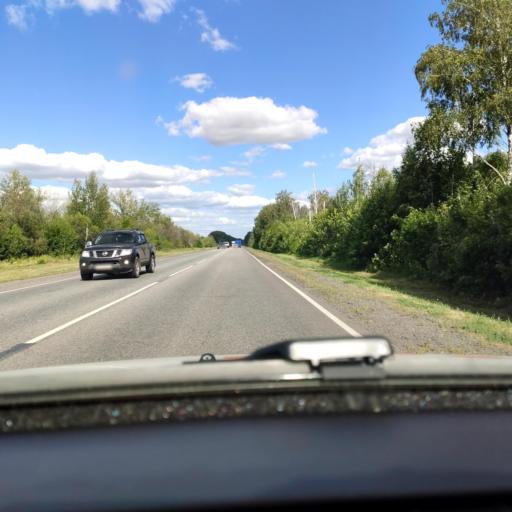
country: RU
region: Voronezj
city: Kashirskoye
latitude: 51.4584
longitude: 39.7699
